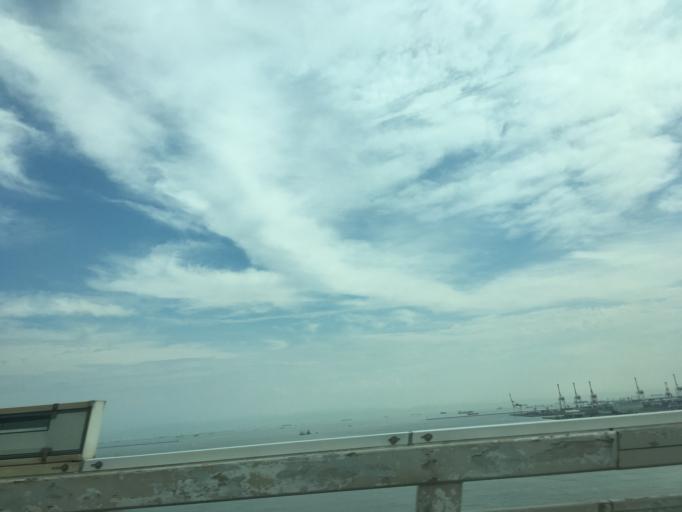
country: JP
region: Hyogo
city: Ashiya
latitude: 34.7097
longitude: 135.2900
